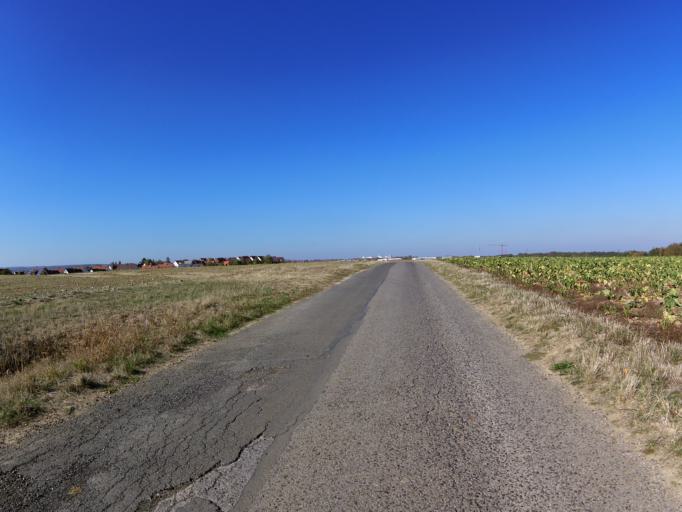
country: DE
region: Bavaria
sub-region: Regierungsbezirk Unterfranken
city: Eibelstadt
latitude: 49.7199
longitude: 9.9786
